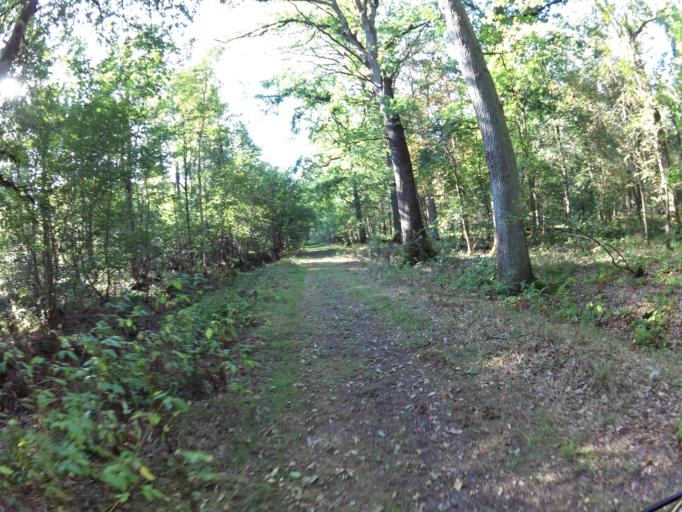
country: DE
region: North Rhine-Westphalia
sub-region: Regierungsbezirk Koln
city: Gangelt
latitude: 50.9761
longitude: 6.0087
